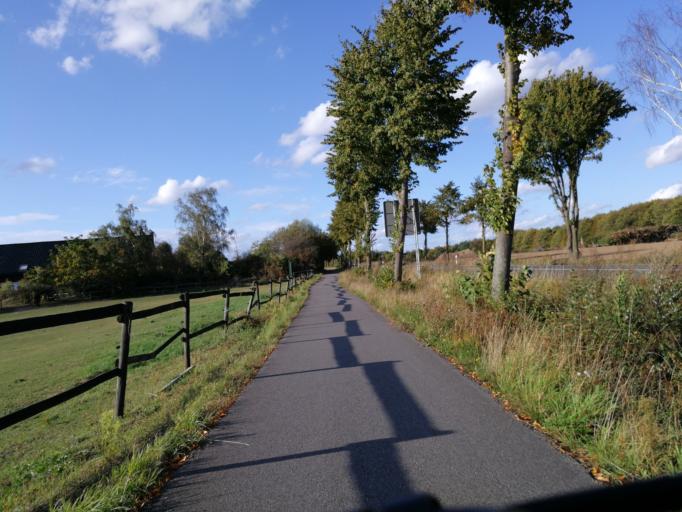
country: DE
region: North Rhine-Westphalia
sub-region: Regierungsbezirk Dusseldorf
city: Neubrueck
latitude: 51.1120
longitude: 6.7147
